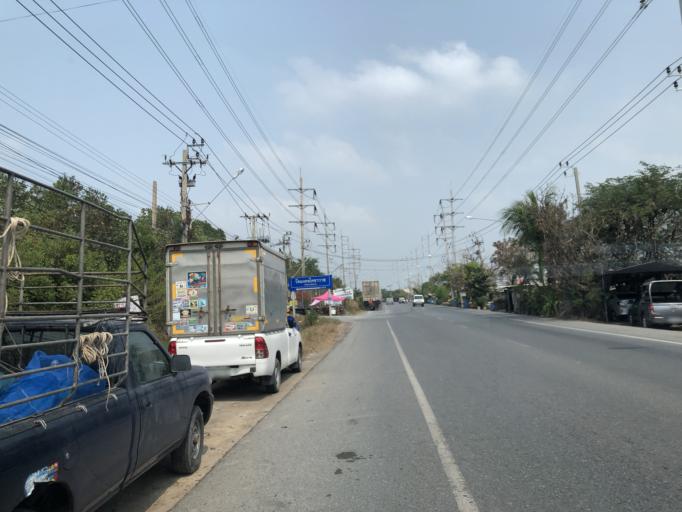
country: TH
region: Samut Prakan
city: Bang Bo
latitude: 13.5169
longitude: 100.8331
